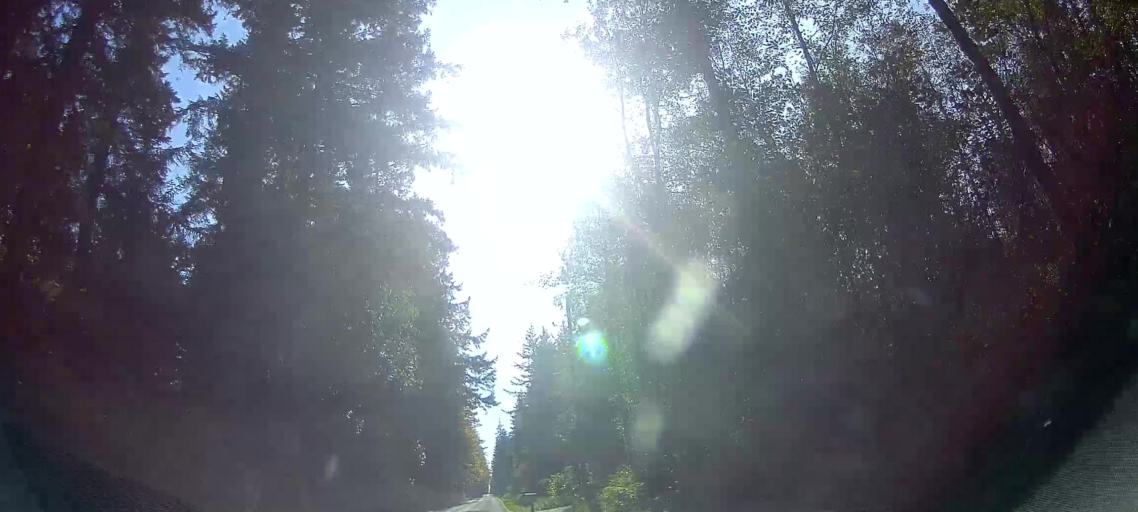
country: US
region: Washington
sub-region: Snohomish County
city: Stanwood
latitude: 48.2258
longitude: -122.4557
